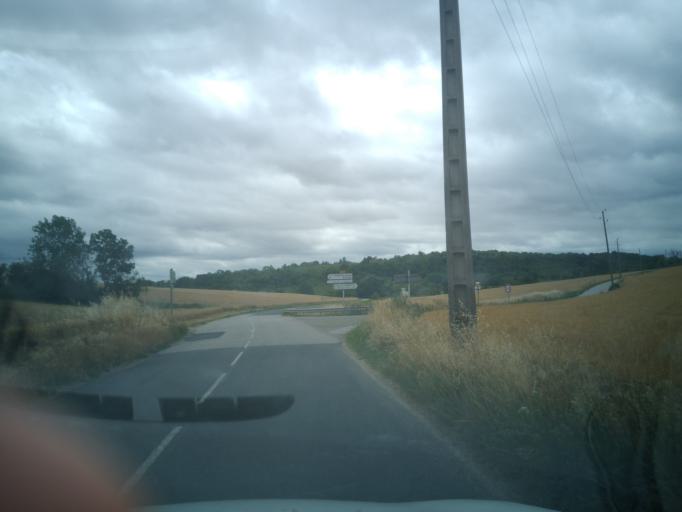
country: FR
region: Ile-de-France
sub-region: Departement des Yvelines
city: Crespieres
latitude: 48.8679
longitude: 1.9140
